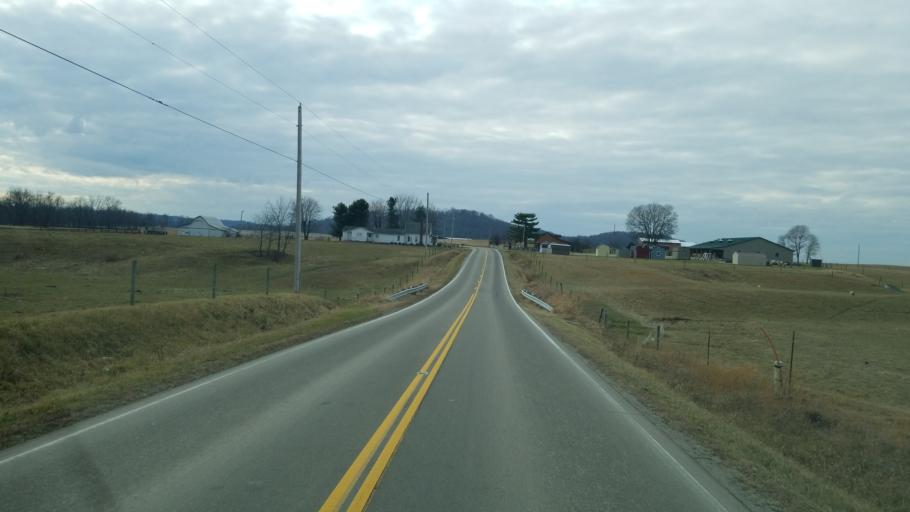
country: US
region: Ohio
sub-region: Highland County
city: Greenfield
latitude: 39.1941
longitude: -83.3261
